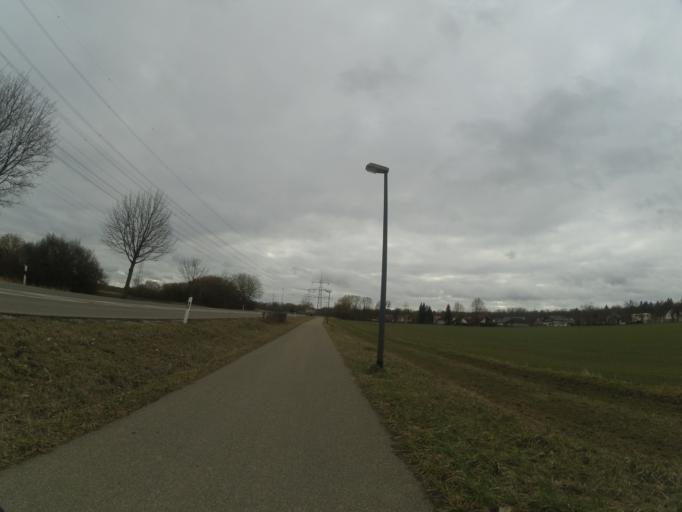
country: DE
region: Baden-Wuerttemberg
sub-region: Tuebingen Region
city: Illerrieden
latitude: 48.2978
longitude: 10.0596
